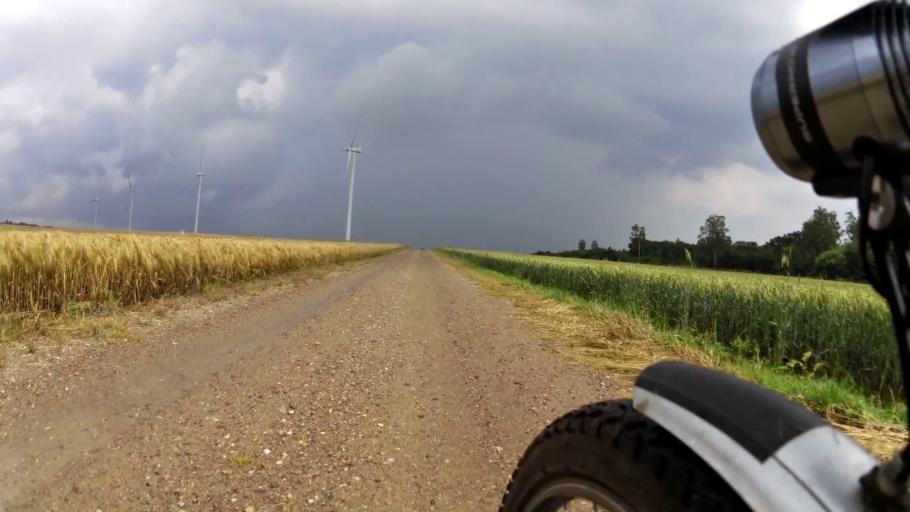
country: PL
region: West Pomeranian Voivodeship
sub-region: Powiat lobeski
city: Lobez
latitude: 53.7111
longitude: 15.6321
